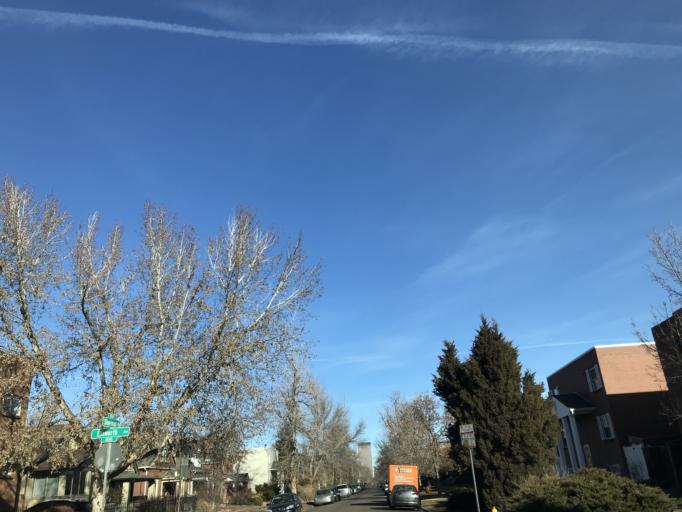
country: US
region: Colorado
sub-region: Denver County
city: Denver
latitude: 39.7165
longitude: -104.9850
